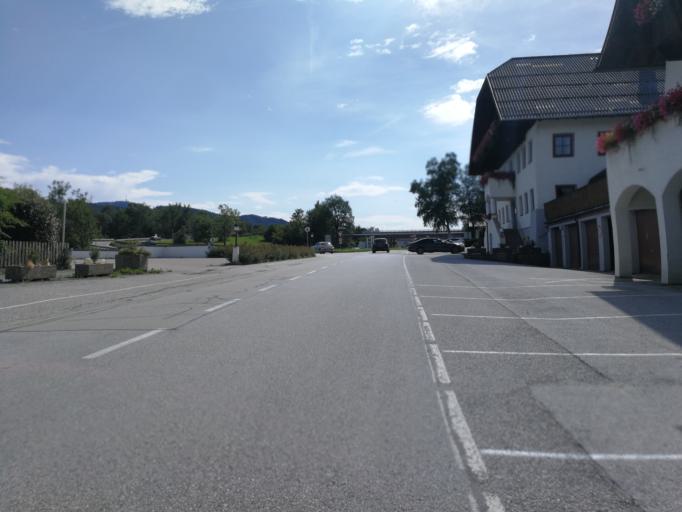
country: AT
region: Salzburg
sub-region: Politischer Bezirk Salzburg-Umgebung
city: Eugendorf
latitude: 47.8680
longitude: 13.1336
